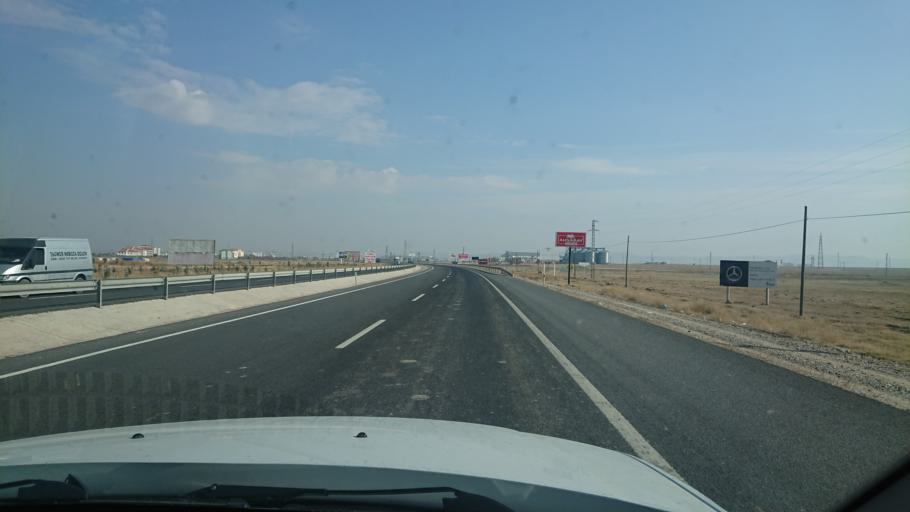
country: TR
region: Aksaray
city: Aksaray
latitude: 38.3371
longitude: 33.9375
